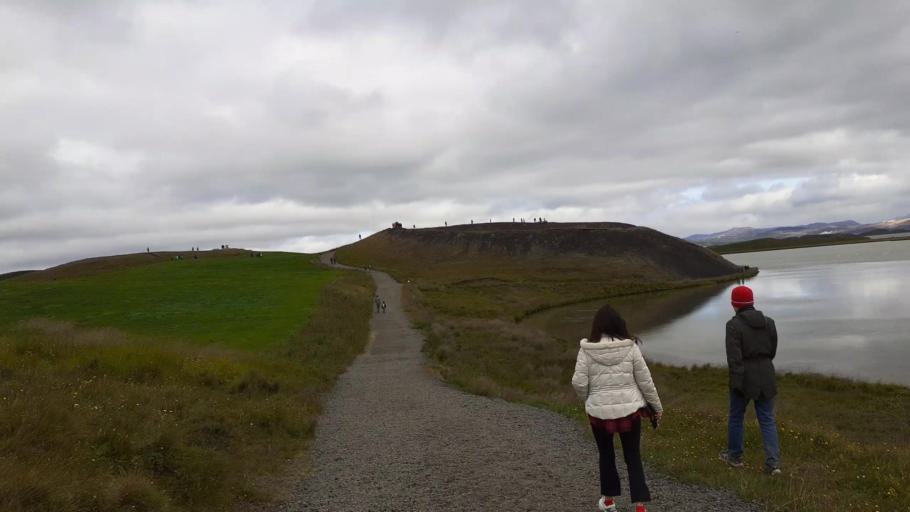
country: IS
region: Northeast
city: Laugar
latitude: 65.5689
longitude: -17.0334
